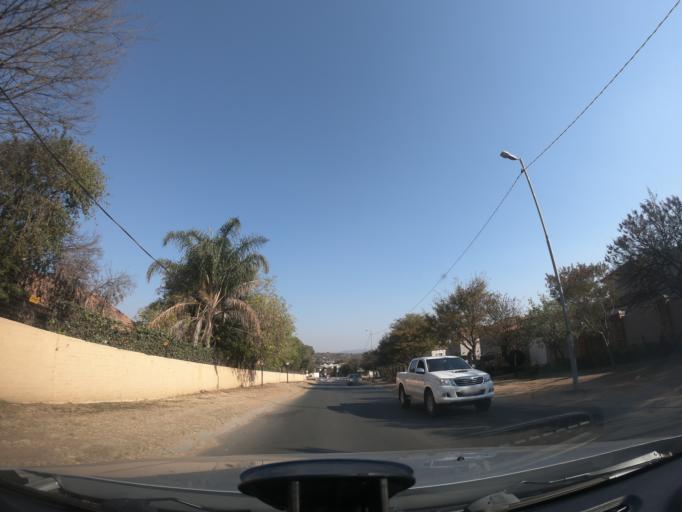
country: ZA
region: Gauteng
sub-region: City of Johannesburg Metropolitan Municipality
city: Diepsloot
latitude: -26.0172
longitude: 27.9965
